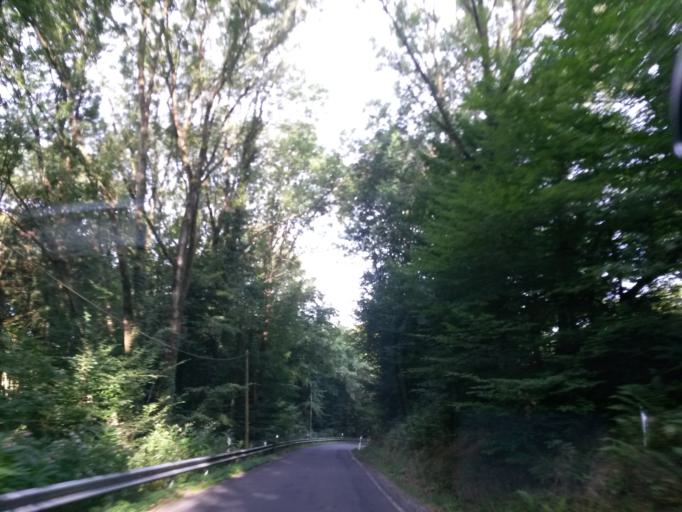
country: DE
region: North Rhine-Westphalia
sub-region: Regierungsbezirk Koln
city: Rosrath
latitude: 50.8838
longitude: 7.2237
